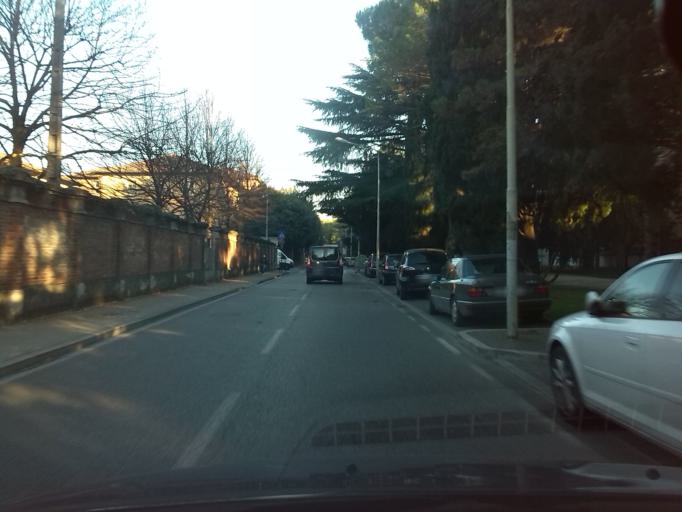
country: IT
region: Friuli Venezia Giulia
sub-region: Provincia di Udine
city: Udine
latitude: 46.0693
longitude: 13.2413
